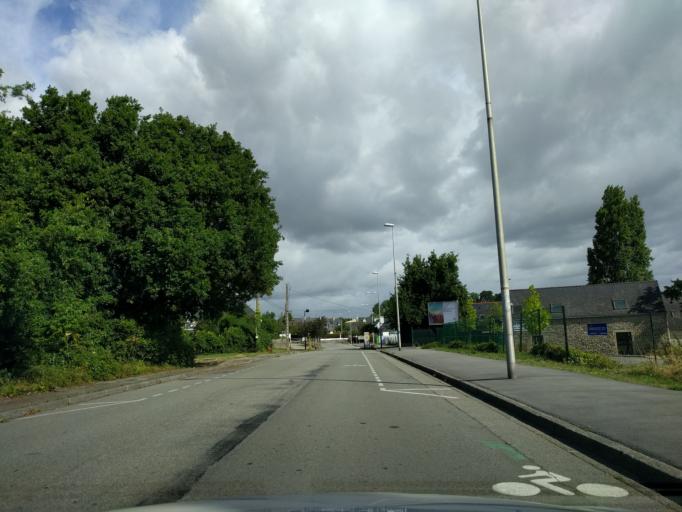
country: FR
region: Brittany
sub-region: Departement du Morbihan
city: Lorient
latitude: 47.7481
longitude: -3.3931
